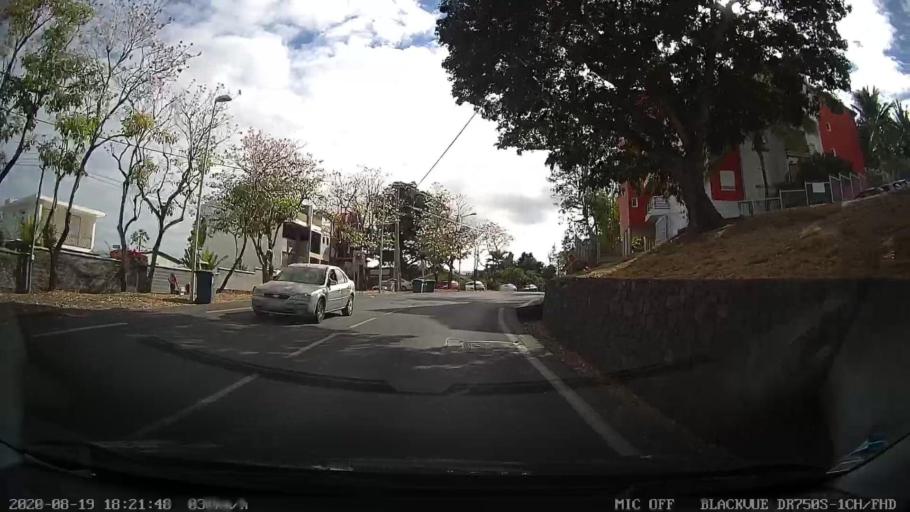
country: RE
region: Reunion
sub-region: Reunion
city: La Possession
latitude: -20.9570
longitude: 55.3366
